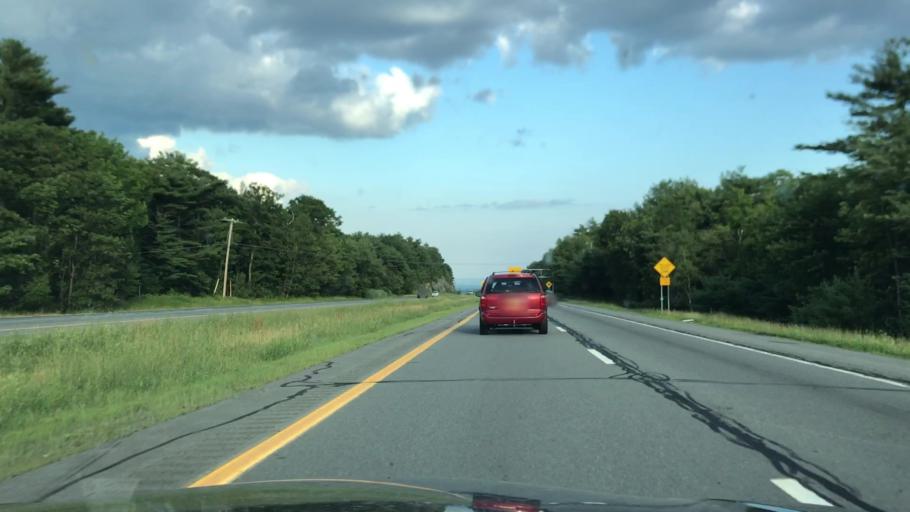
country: US
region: New York
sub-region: Sullivan County
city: Rock Hill
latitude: 41.5979
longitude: -74.5455
